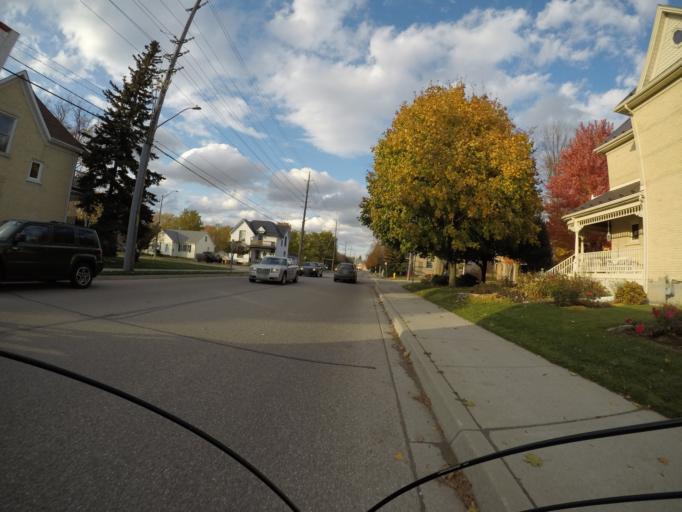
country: CA
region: Ontario
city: Waterloo
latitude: 43.5972
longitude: -80.5636
